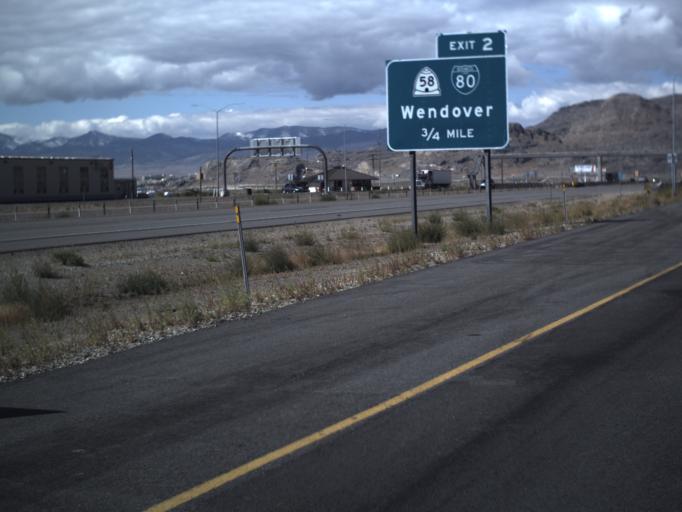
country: US
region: Utah
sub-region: Tooele County
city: Wendover
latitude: 40.7449
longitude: -113.9876
